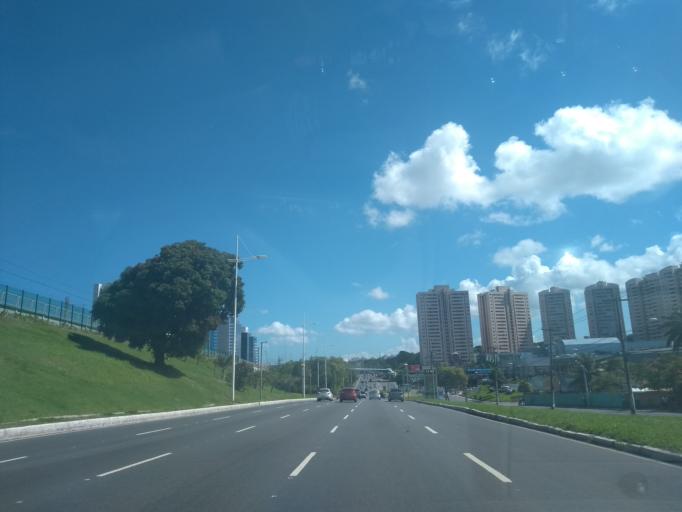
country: BR
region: Bahia
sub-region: Lauro De Freitas
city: Lauro de Freitas
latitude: -12.9379
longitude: -38.4075
